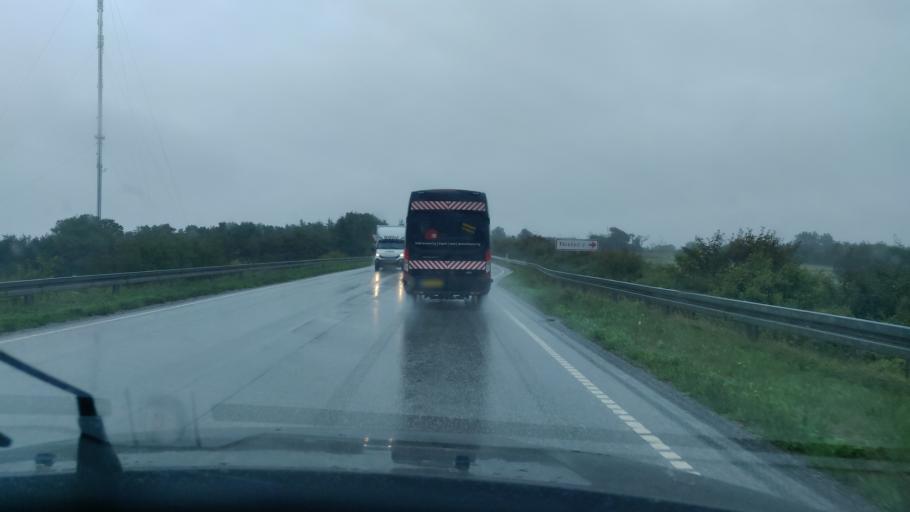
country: DK
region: North Denmark
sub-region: Thisted Kommune
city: Thisted
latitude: 56.9744
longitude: 8.6769
